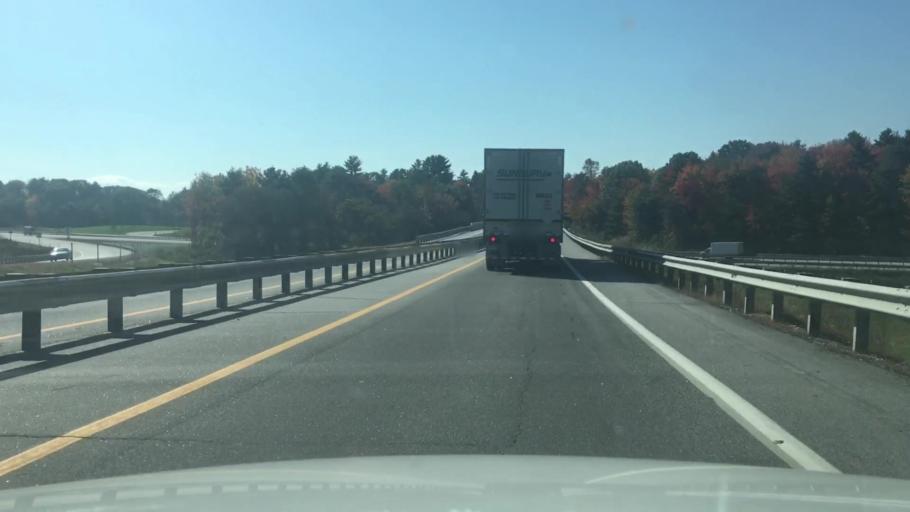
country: US
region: Maine
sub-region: Cumberland County
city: Falmouth
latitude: 43.7223
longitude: -70.3029
